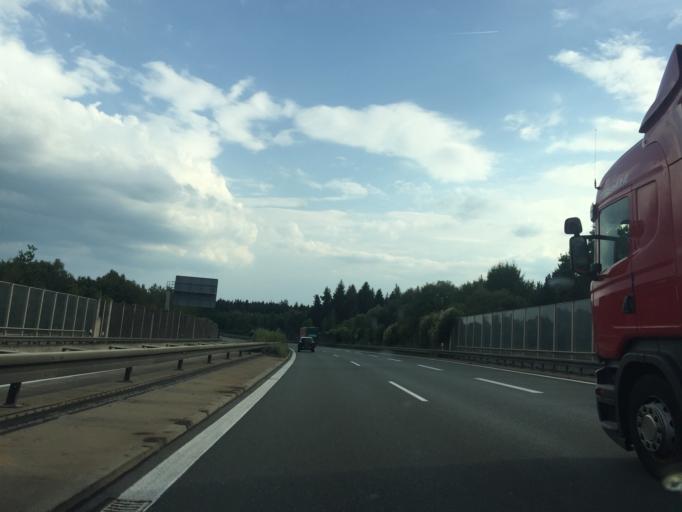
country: DE
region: Bavaria
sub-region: Upper Palatinate
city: Weiden
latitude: 49.6847
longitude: 12.1277
